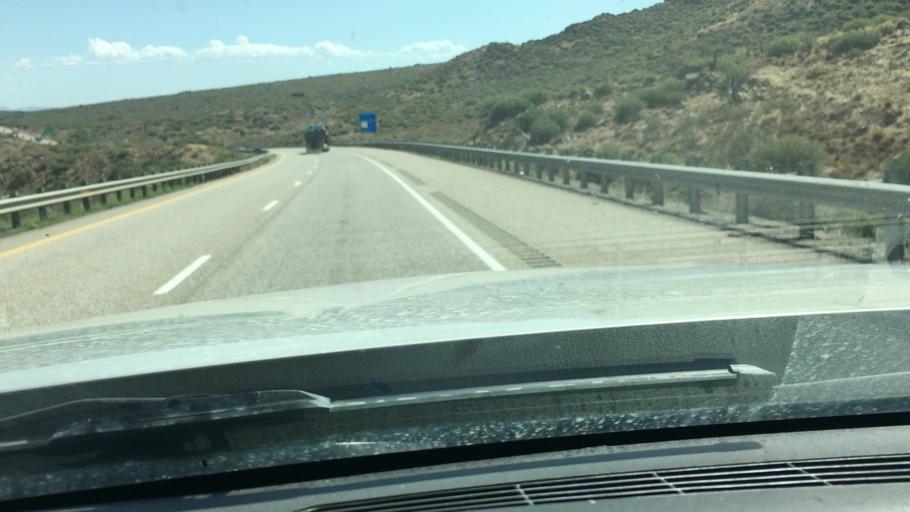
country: US
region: Utah
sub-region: Washington County
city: Toquerville
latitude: 37.3089
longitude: -113.2973
